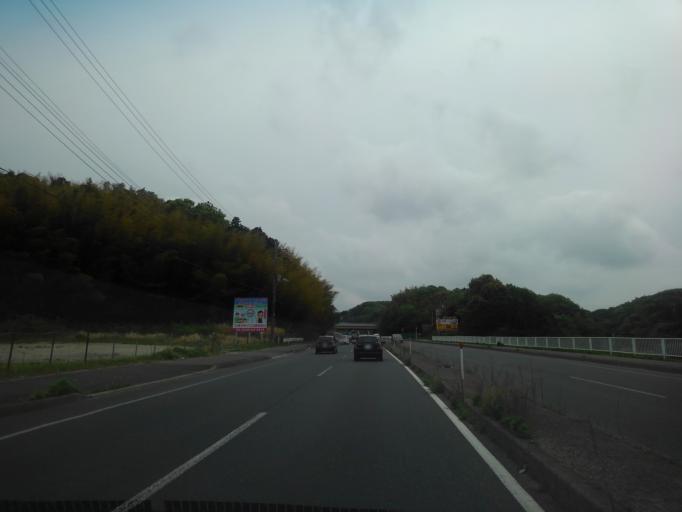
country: JP
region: Chiba
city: Kisarazu
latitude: 35.3533
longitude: 139.9204
